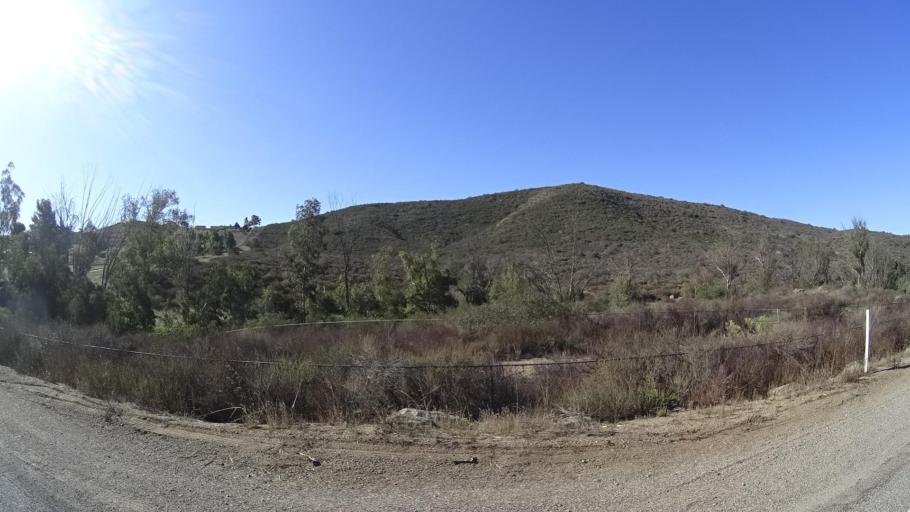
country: US
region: California
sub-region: San Diego County
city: Jamul
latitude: 32.6653
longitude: -116.7962
